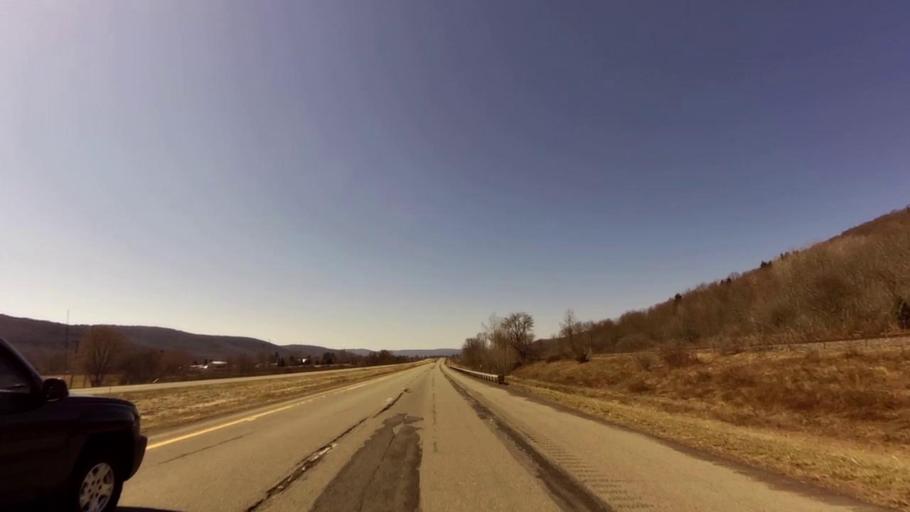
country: US
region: New York
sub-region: Cattaraugus County
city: Franklinville
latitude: 42.3128
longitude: -78.4605
